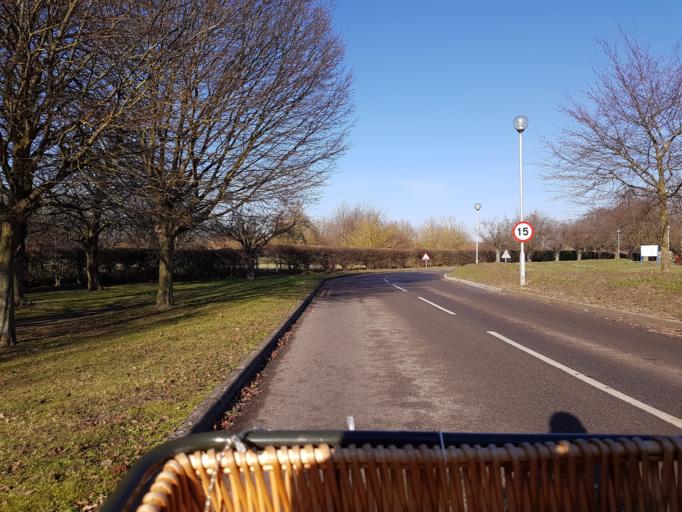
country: GB
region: England
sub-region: Cambridgeshire
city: Fulbourn
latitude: 52.1840
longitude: 0.1860
